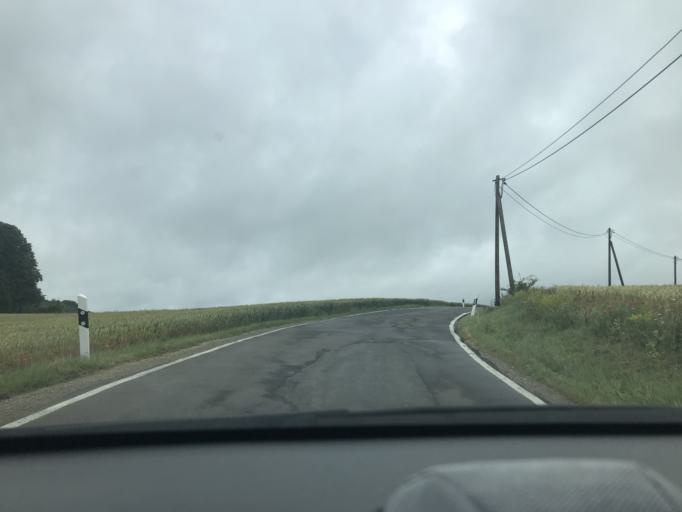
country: DE
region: Thuringia
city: Geisleden
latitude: 51.3218
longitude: 10.1923
